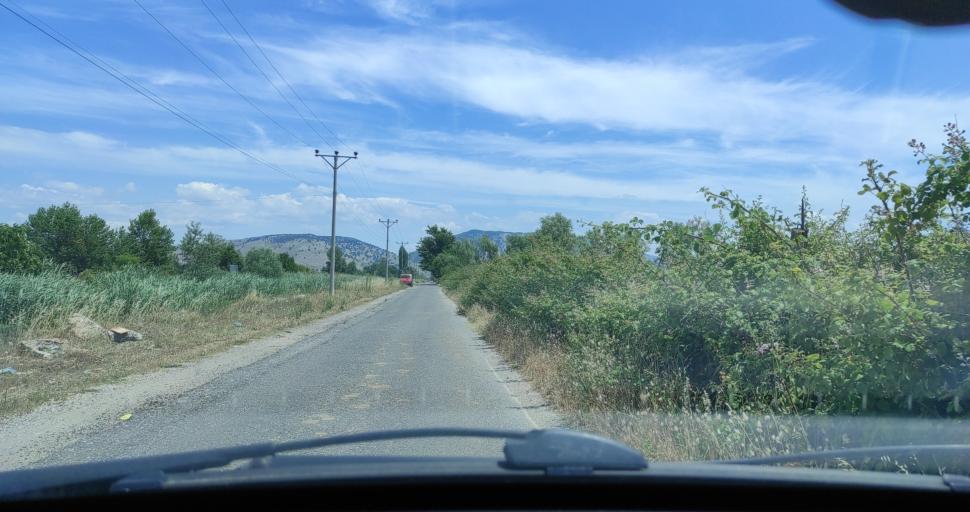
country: AL
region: Shkoder
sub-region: Rrethi i Shkodres
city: Velipoje
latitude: 41.8788
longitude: 19.3949
